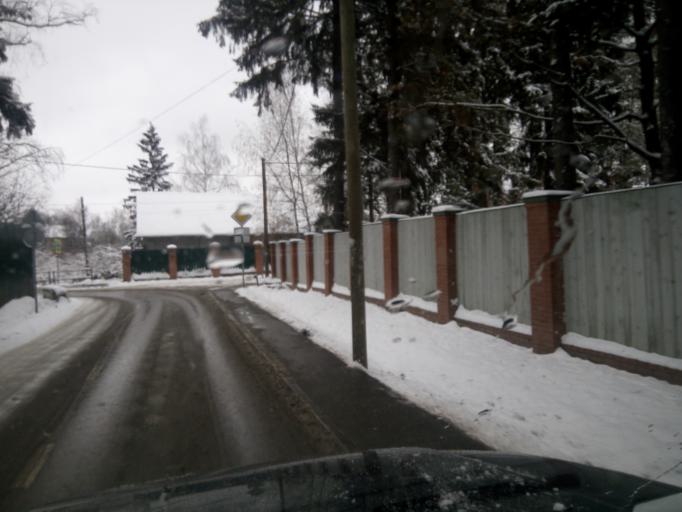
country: RU
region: Moskovskaya
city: Skhodnya
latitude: 55.9504
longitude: 37.3109
